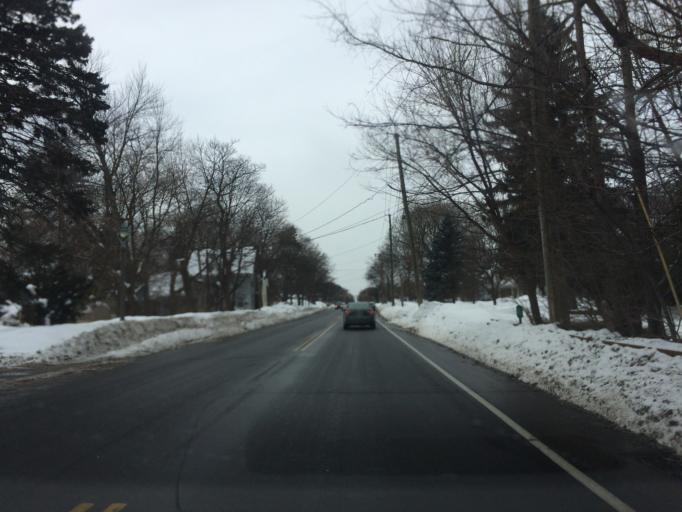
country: US
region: New York
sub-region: Monroe County
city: Brighton
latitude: 43.1266
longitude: -77.5612
